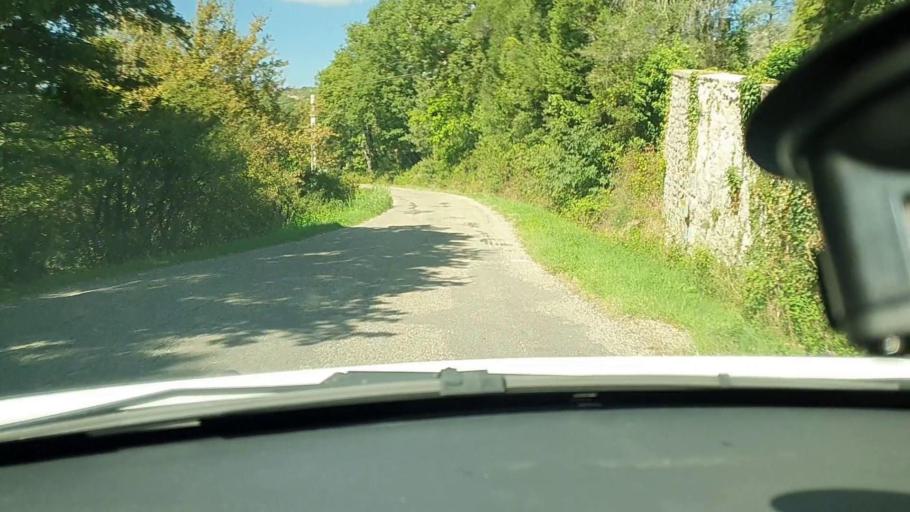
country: FR
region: Languedoc-Roussillon
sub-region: Departement du Gard
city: Goudargues
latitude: 44.1693
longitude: 4.3888
